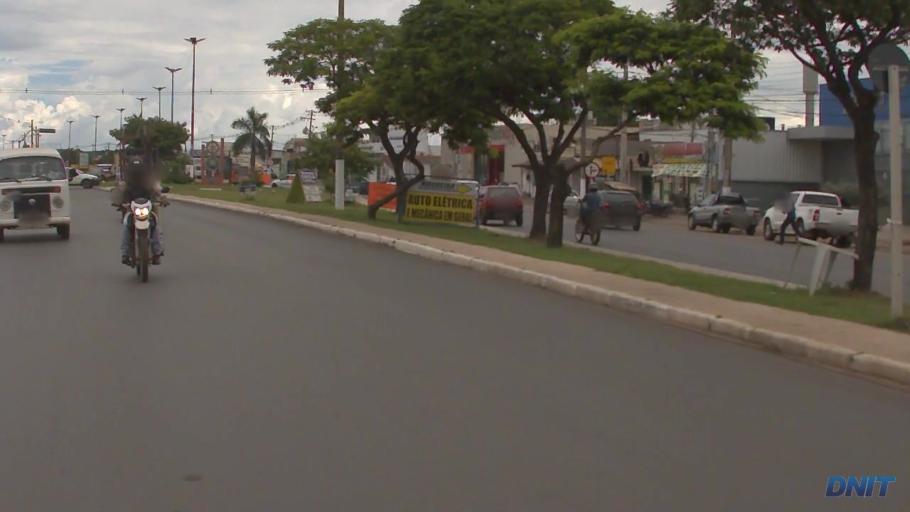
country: BR
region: Mato Grosso
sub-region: Varzea Grande
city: Varzea Grande
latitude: -15.6416
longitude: -56.1752
